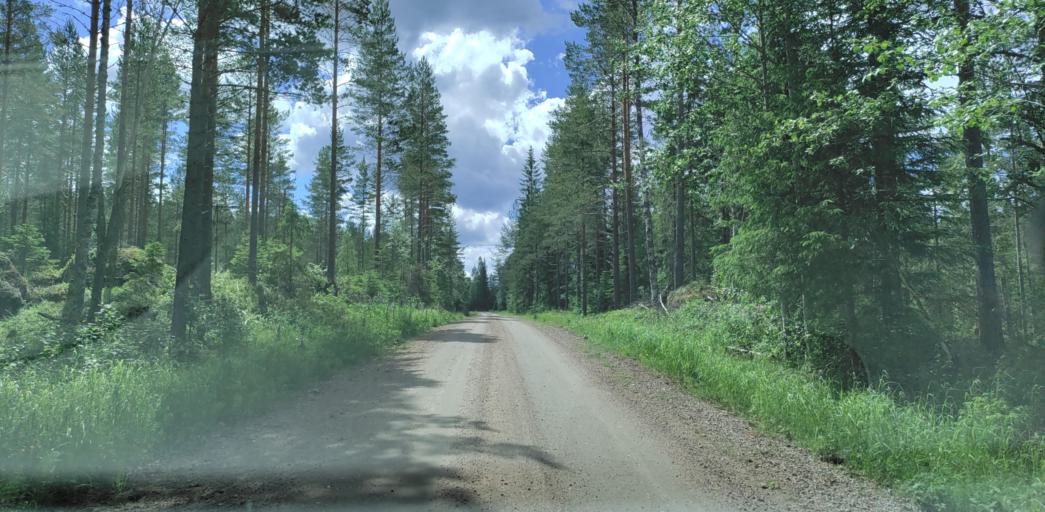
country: SE
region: Vaermland
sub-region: Hagfors Kommun
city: Ekshaerad
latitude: 60.0981
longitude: 13.3487
